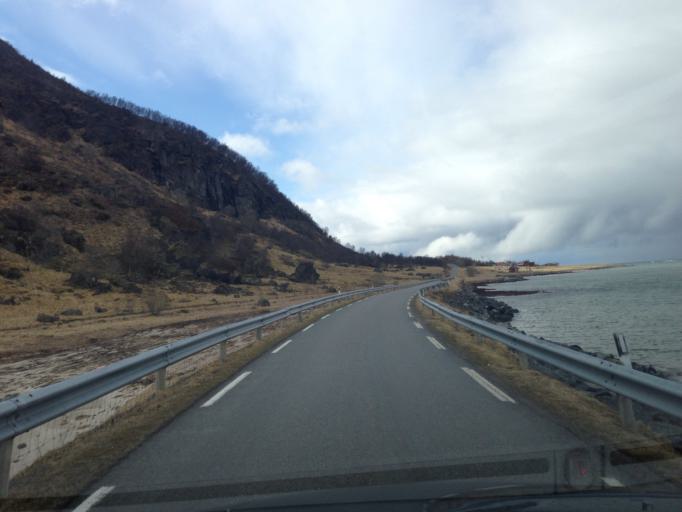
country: NO
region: Nordland
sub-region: Vagan
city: Svolvaer
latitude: 68.3960
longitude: 14.5367
